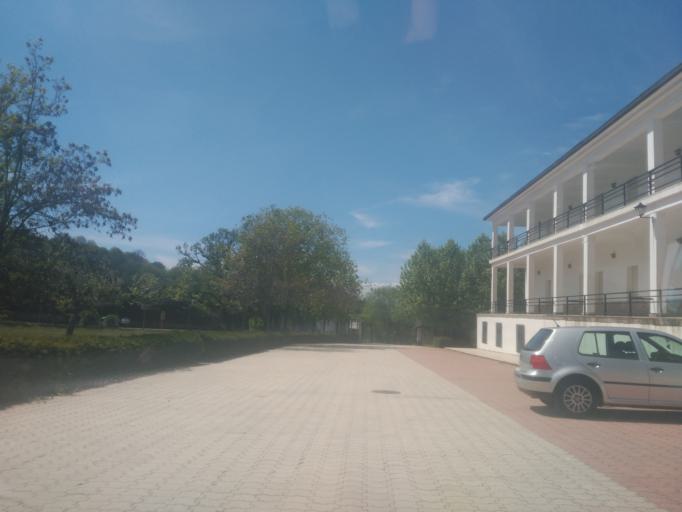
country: ES
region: Castille and Leon
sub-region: Provincia de Salamanca
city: Bejar
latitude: 40.3752
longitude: -5.7625
